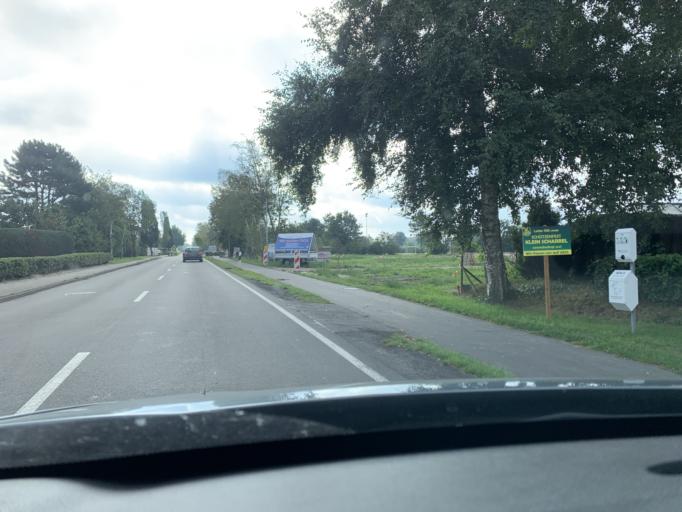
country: DE
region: Lower Saxony
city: Edewecht
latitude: 53.1014
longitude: 8.0777
